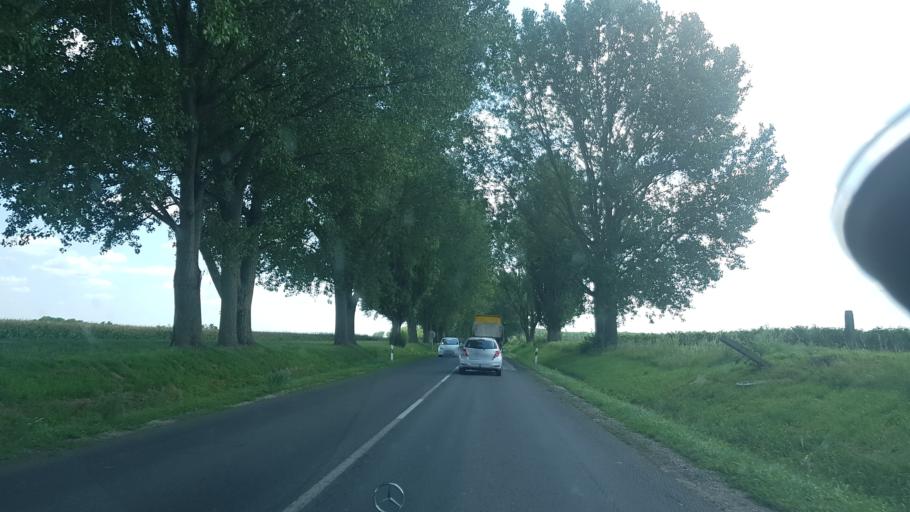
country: HU
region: Somogy
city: Kethely
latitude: 46.6311
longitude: 17.3959
